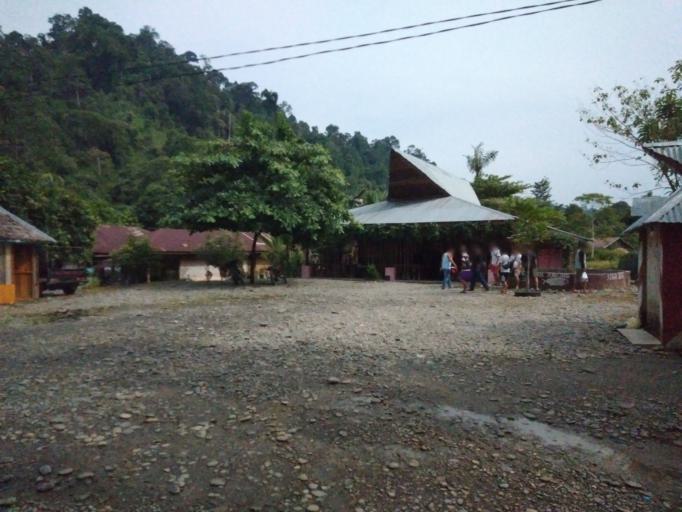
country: ID
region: Aceh
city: Tenggulun
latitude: 3.6966
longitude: 98.0695
